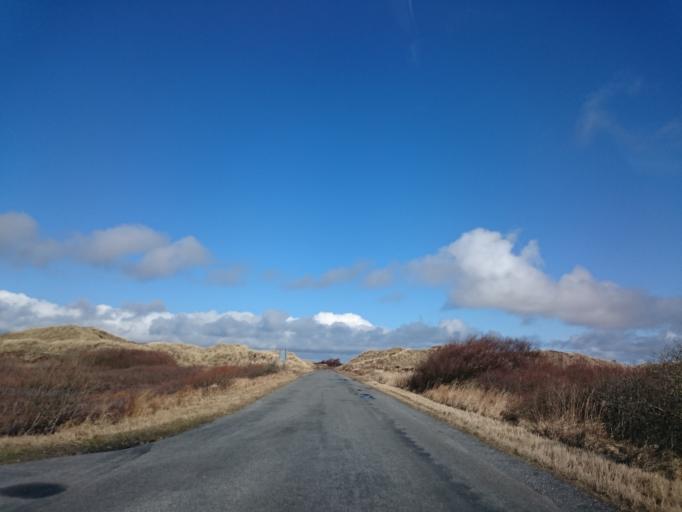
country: DK
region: North Denmark
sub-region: Frederikshavn Kommune
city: Strandby
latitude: 57.6556
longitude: 10.4096
